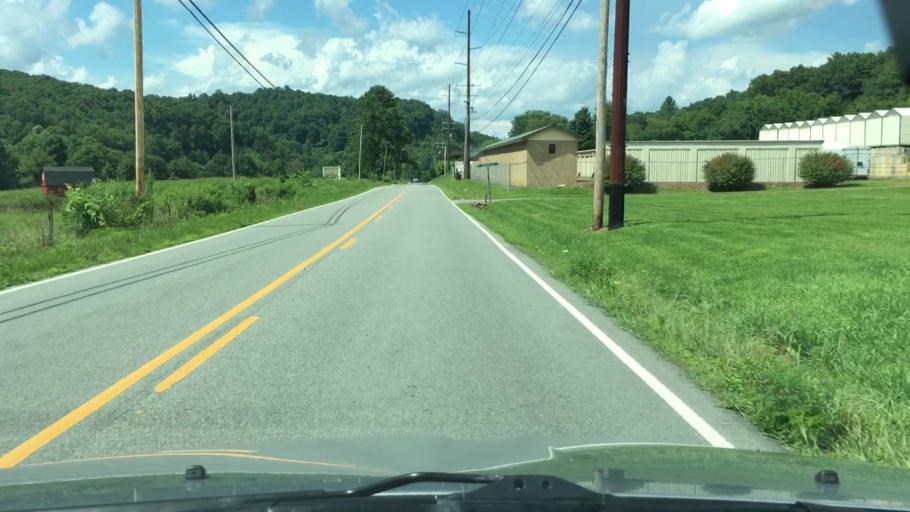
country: US
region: North Carolina
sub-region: Yancey County
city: Burnsville
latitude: 35.8894
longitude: -82.2147
